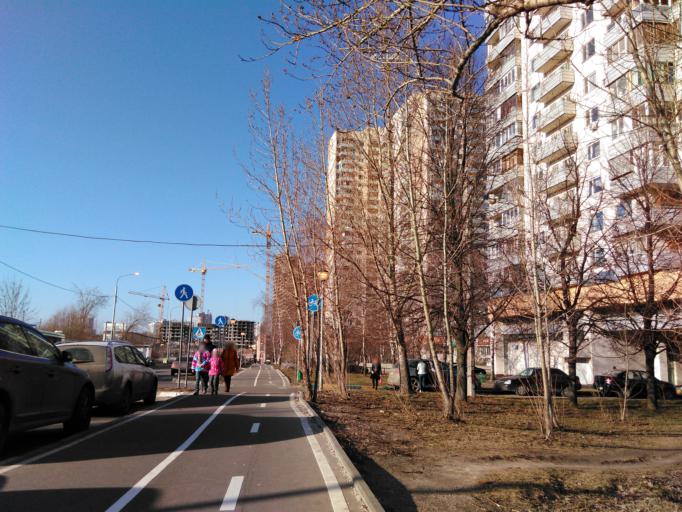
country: RU
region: Moscow
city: Kotlovka
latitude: 55.6370
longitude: 37.5896
